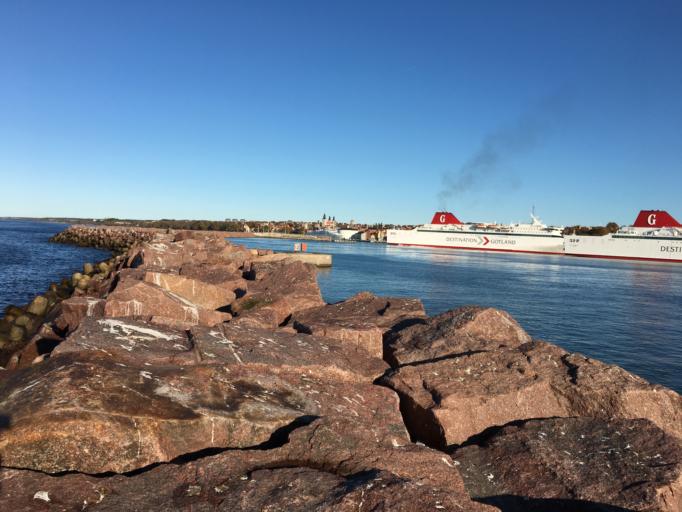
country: SE
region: Gotland
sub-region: Gotland
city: Visby
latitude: 57.6350
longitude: 18.2701
